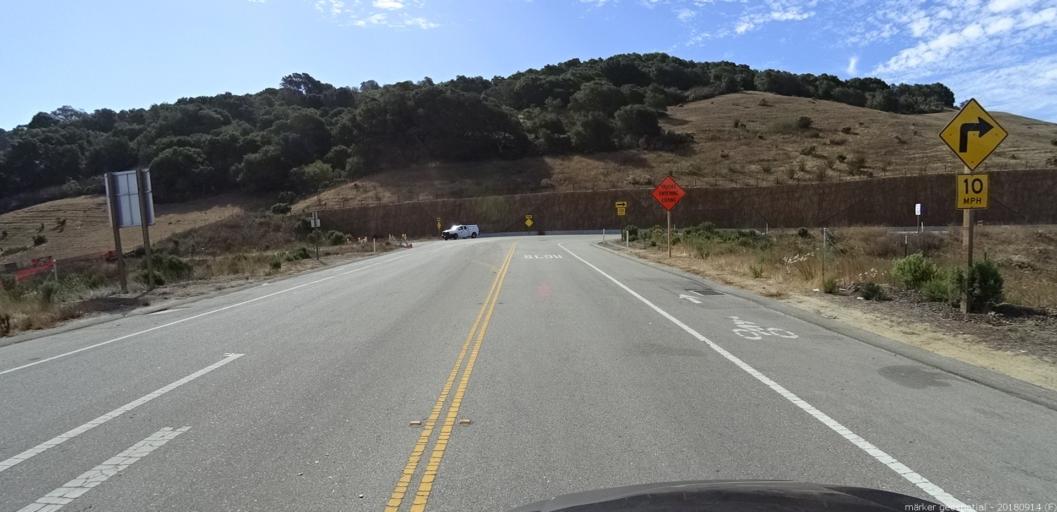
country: US
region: California
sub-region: San Benito County
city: Aromas
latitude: 36.8566
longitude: -121.6271
